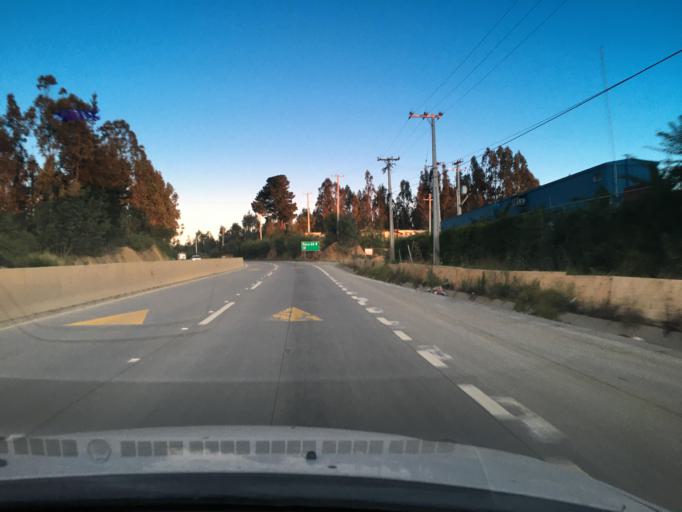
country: CL
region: Valparaiso
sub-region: Provincia de Valparaiso
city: Valparaiso
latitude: -33.0950
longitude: -71.6004
